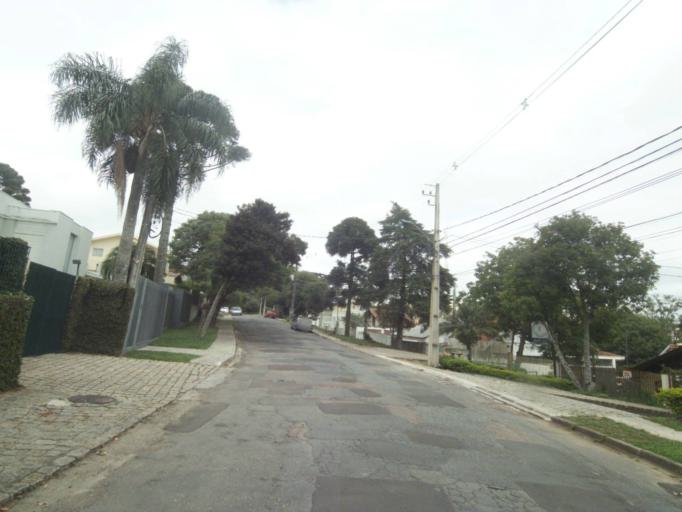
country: BR
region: Parana
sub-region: Curitiba
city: Curitiba
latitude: -25.3930
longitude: -49.2799
